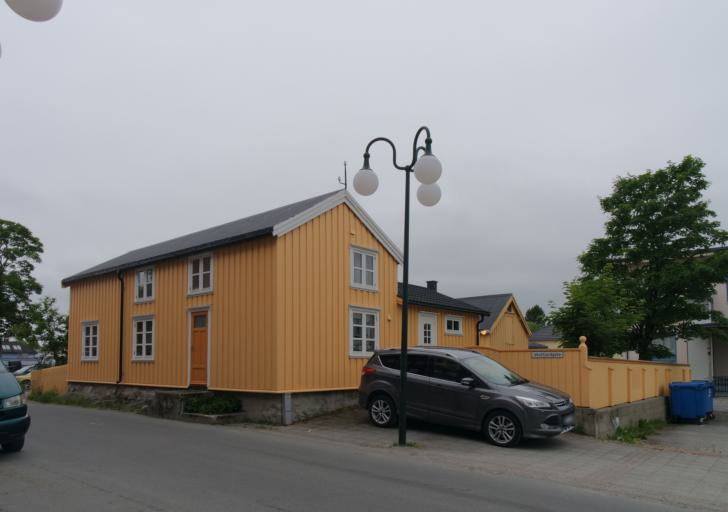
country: NO
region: Nordland
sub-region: Vagan
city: Svolvaer
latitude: 68.2339
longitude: 14.5666
